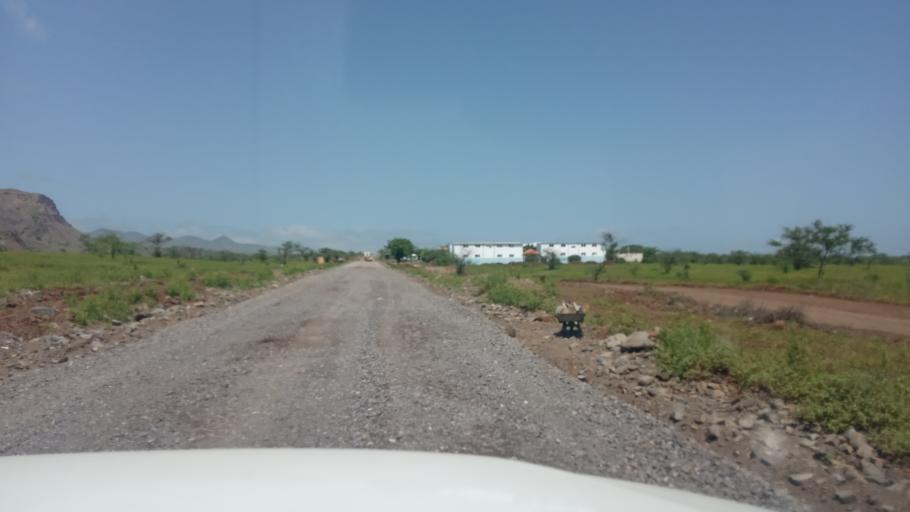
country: CV
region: Ribeira Grande de Santiago
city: Cidade Velha
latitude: 14.9239
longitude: -23.6112
